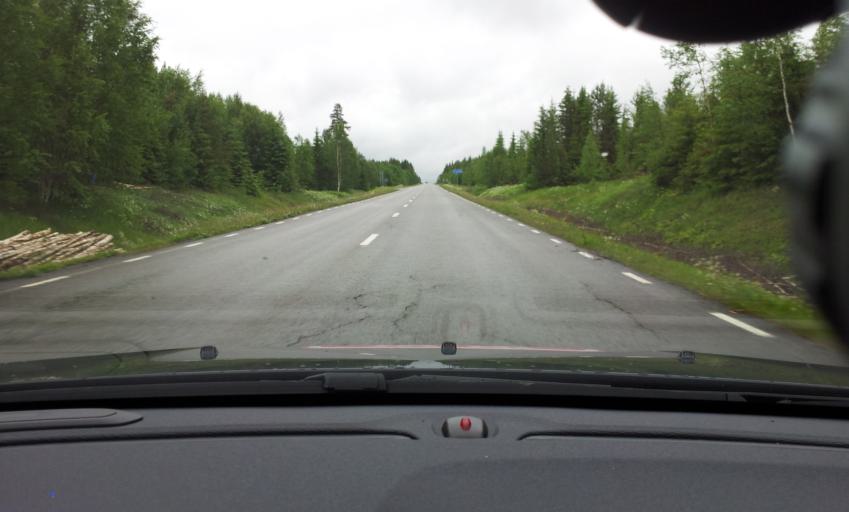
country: SE
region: Jaemtland
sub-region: Krokoms Kommun
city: Krokom
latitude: 63.4181
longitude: 14.4935
